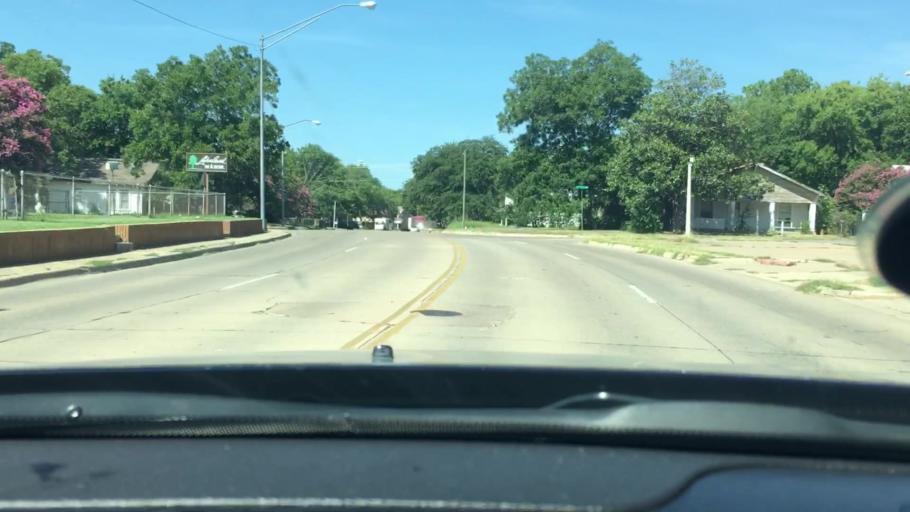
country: US
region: Oklahoma
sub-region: Carter County
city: Ardmore
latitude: 34.1631
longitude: -97.1233
